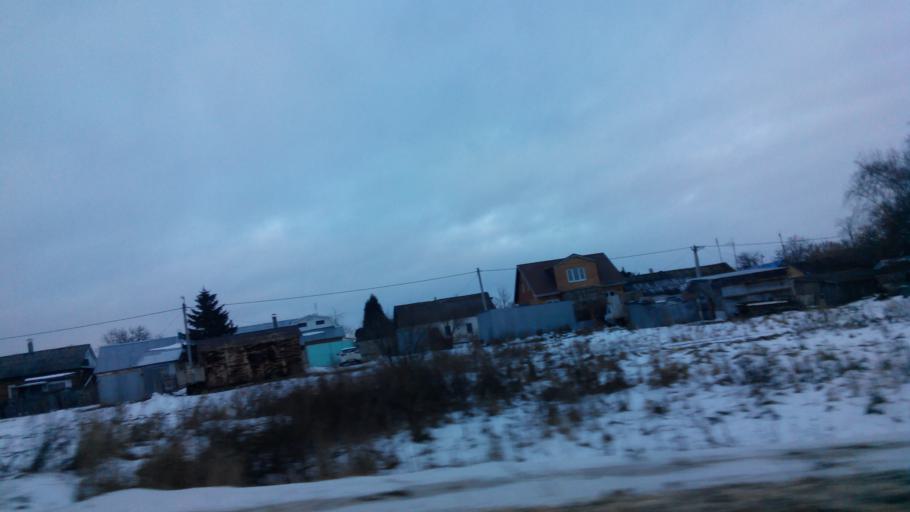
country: RU
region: Tula
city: Mayskiy
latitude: 53.9728
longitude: 38.2464
